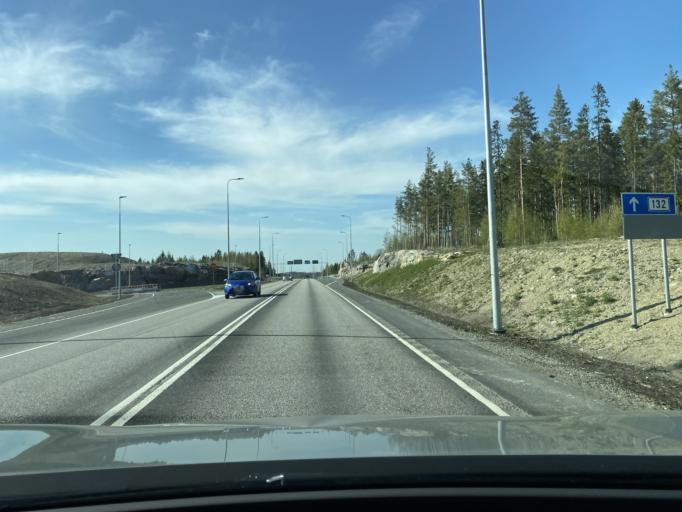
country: FI
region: Uusimaa
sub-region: Helsinki
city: Nurmijaervi
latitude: 60.3870
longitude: 24.7878
